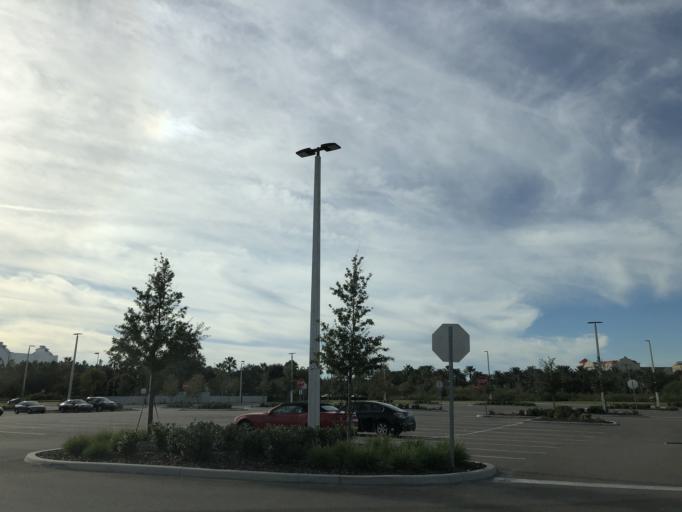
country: US
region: Florida
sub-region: Orange County
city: Tangelo Park
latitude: 28.4350
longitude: -81.4646
